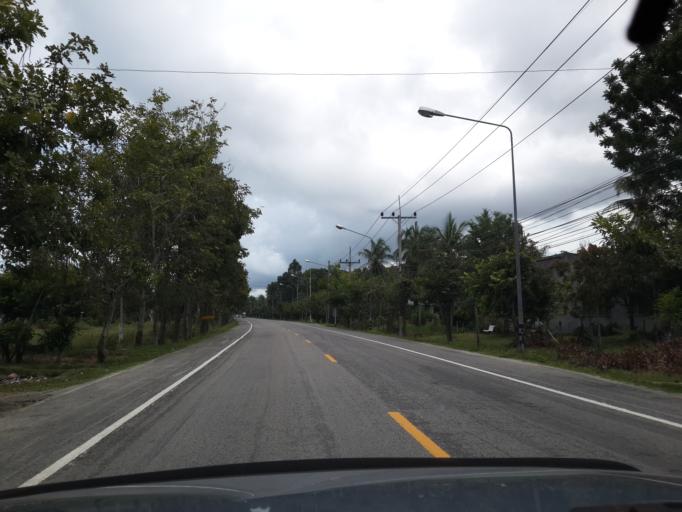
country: TH
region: Narathiwat
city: Narathiwat
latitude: 6.4887
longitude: 101.7766
